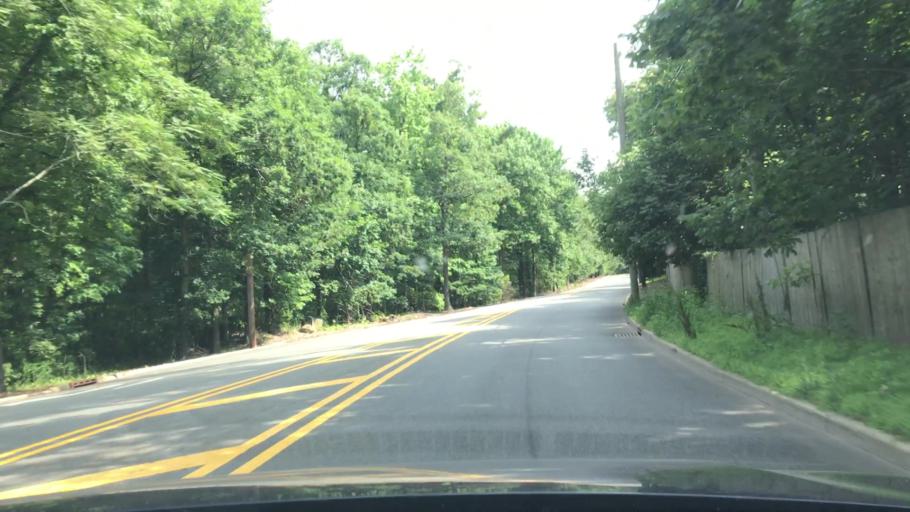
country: US
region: New Jersey
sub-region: Bergen County
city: Tenafly
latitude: 40.9104
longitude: -73.9448
